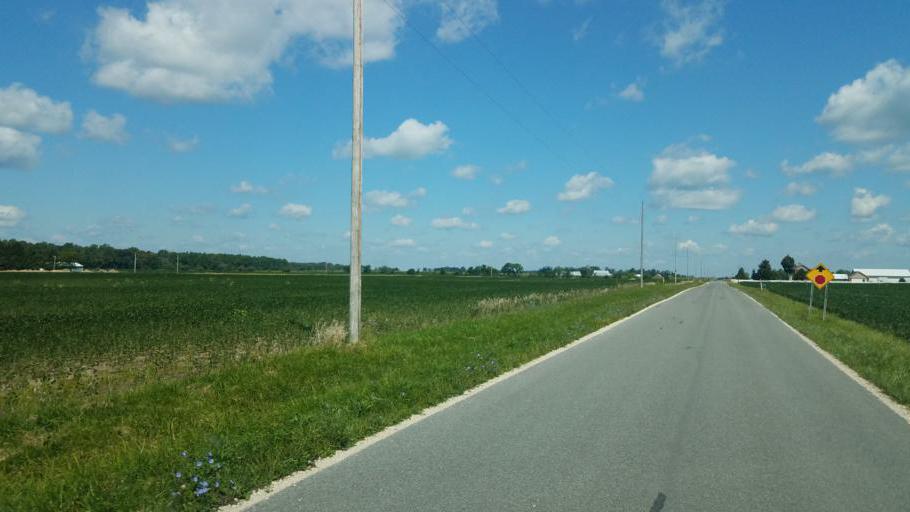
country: US
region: Ohio
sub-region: Wyandot County
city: Carey
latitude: 41.0262
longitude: -83.3244
